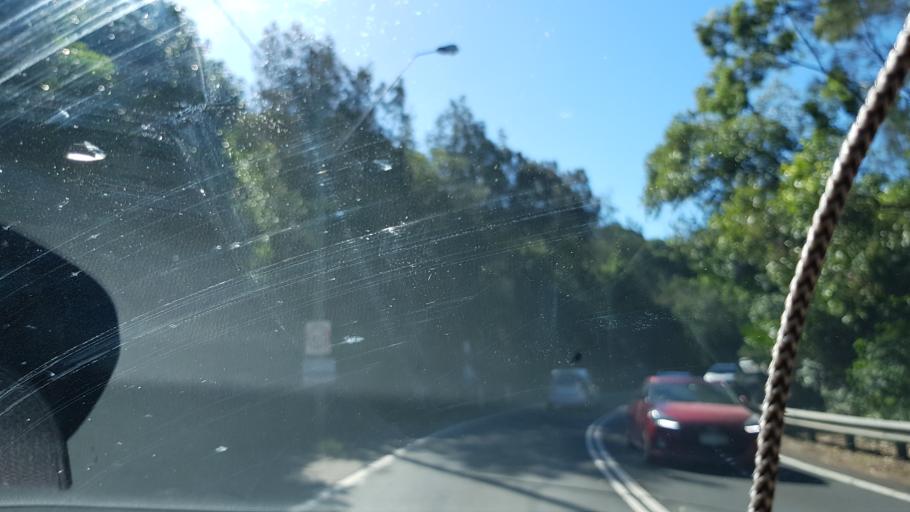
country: AU
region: New South Wales
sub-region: Pittwater
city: Bilgola Beach
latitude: -33.6465
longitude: 151.3249
